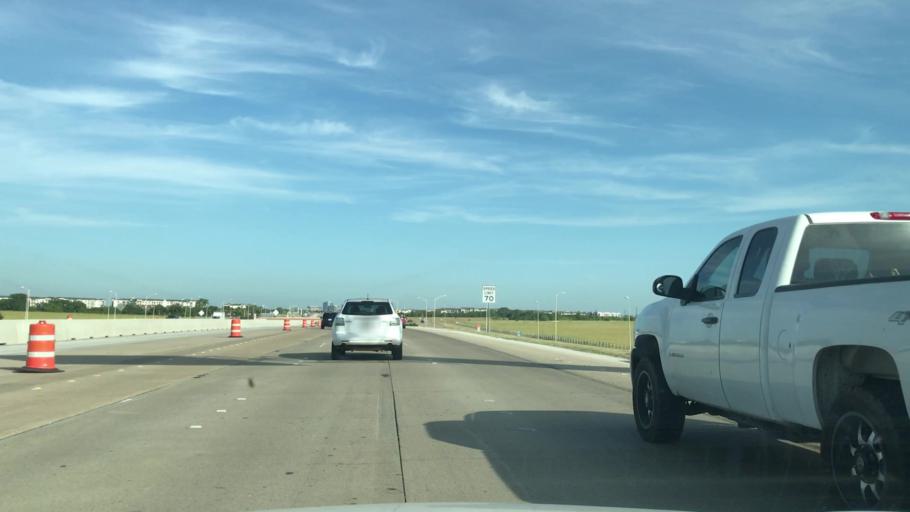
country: US
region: Texas
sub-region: Dallas County
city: Sachse
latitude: 32.9664
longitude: -96.6422
